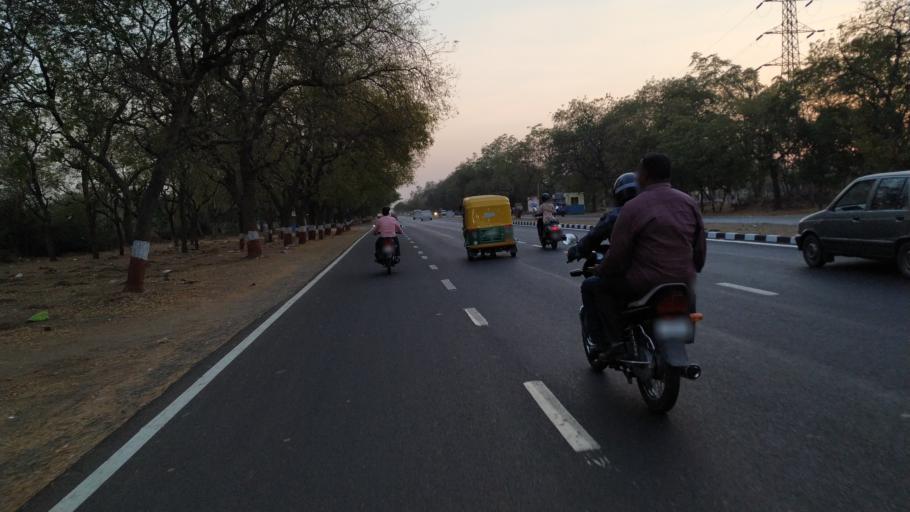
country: IN
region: Gujarat
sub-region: Gandhinagar
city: Adalaj
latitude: 23.1234
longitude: 72.6200
